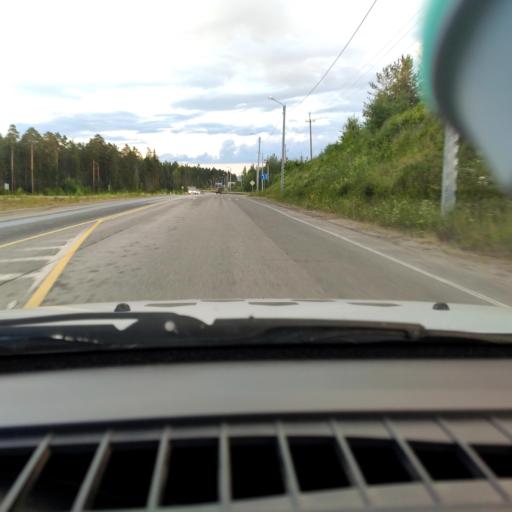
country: RU
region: Chelyabinsk
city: Kyshtym
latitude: 55.7123
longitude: 60.5093
